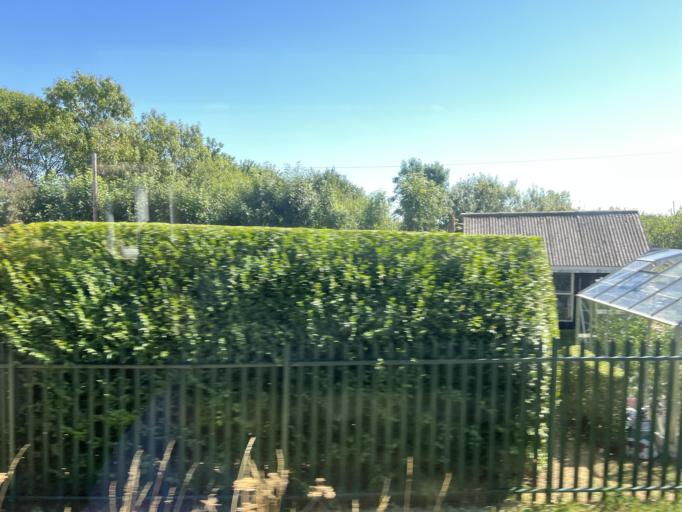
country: GB
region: England
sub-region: Lincolnshire
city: Spilsby
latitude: 53.0906
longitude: 0.0982
